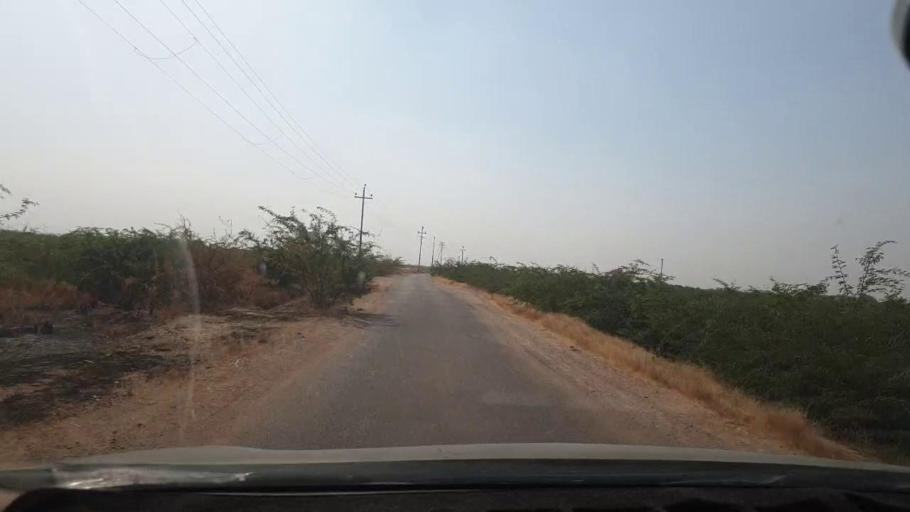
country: PK
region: Sindh
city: Malir Cantonment
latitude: 25.1091
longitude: 67.2031
